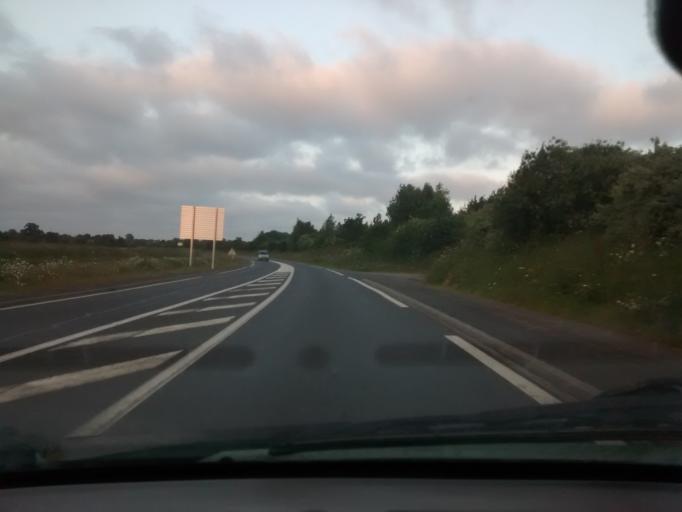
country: FR
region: Lower Normandy
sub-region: Departement de la Manche
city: Agneaux
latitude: 49.0985
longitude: -1.1095
